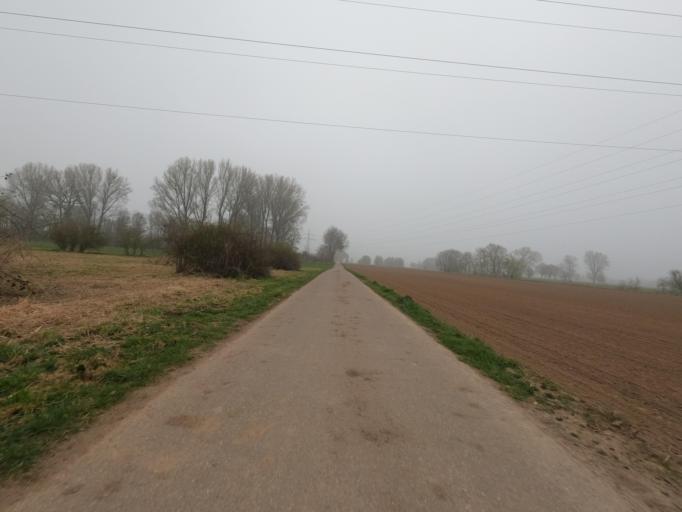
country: DE
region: North Rhine-Westphalia
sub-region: Regierungsbezirk Koln
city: Wassenberg
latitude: 51.0675
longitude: 6.1523
